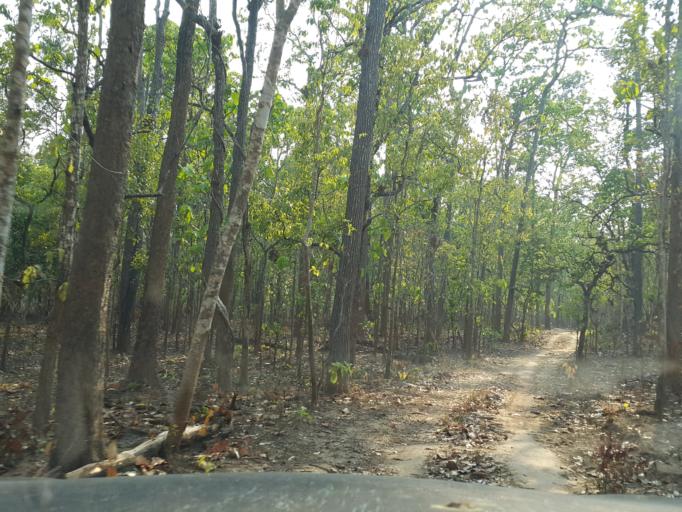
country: TH
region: Lamphun
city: Li
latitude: 17.6139
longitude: 98.8912
